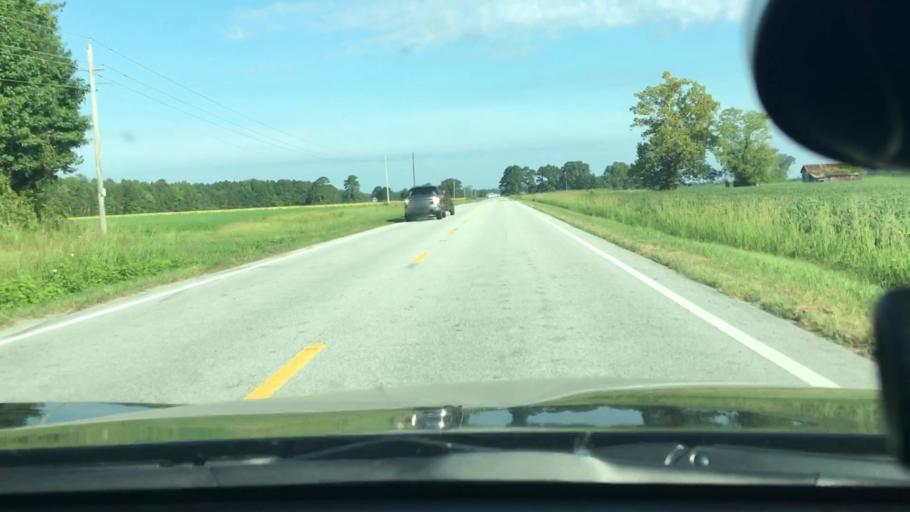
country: US
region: North Carolina
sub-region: Pitt County
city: Summerfield
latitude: 35.6629
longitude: -77.4750
